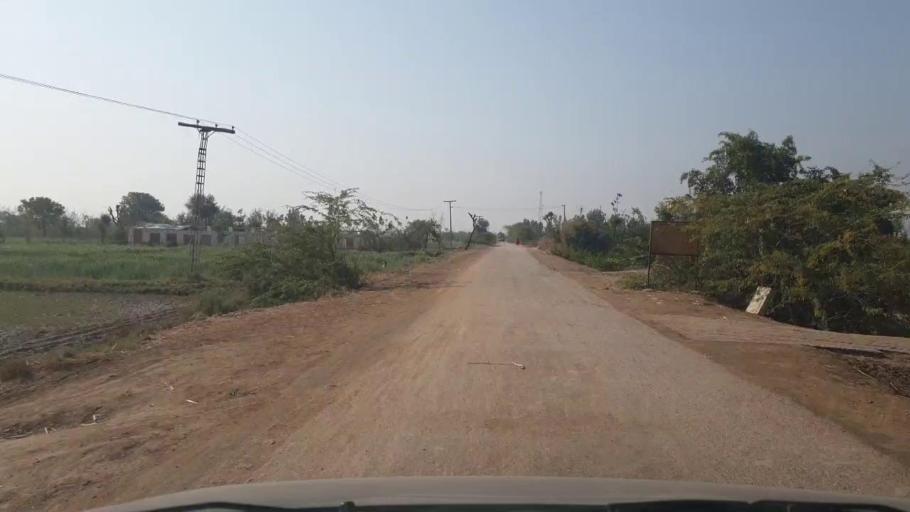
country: PK
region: Sindh
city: Mirwah Gorchani
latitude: 25.3028
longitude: 69.1490
